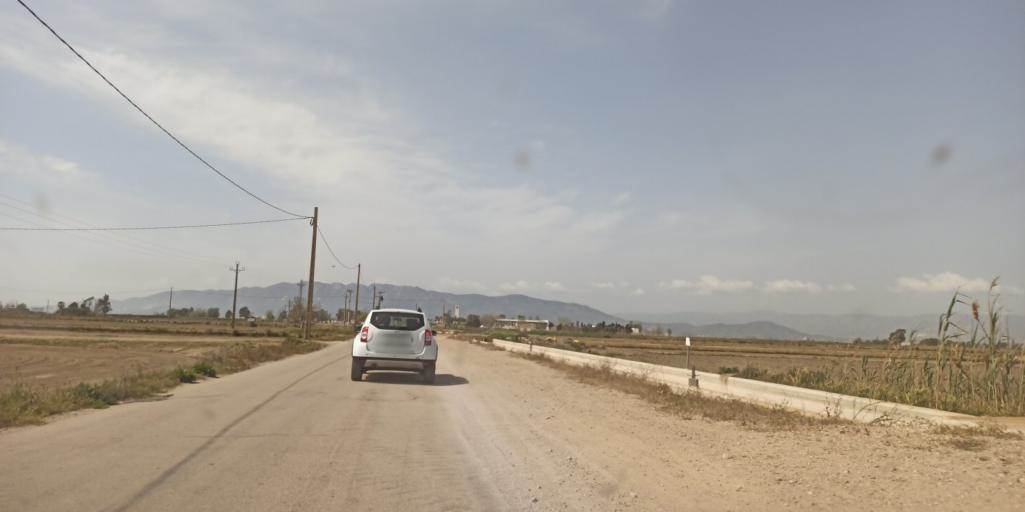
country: ES
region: Catalonia
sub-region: Provincia de Tarragona
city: Deltebre
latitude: 40.6460
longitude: 0.6969
